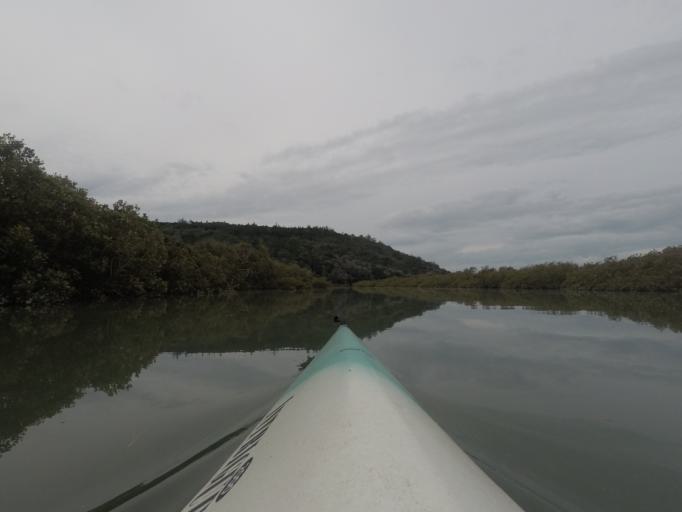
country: NZ
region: Auckland
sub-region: Auckland
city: Rothesay Bay
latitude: -36.6764
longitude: 174.7088
